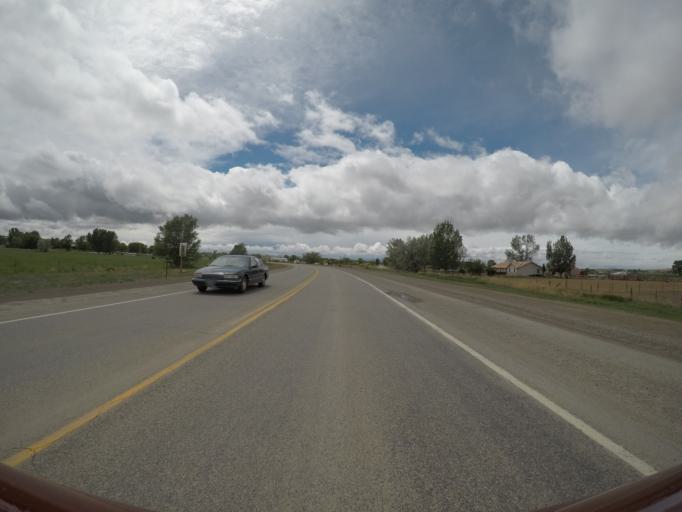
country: US
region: Wyoming
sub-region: Big Horn County
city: Lovell
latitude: 44.8406
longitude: -108.3741
